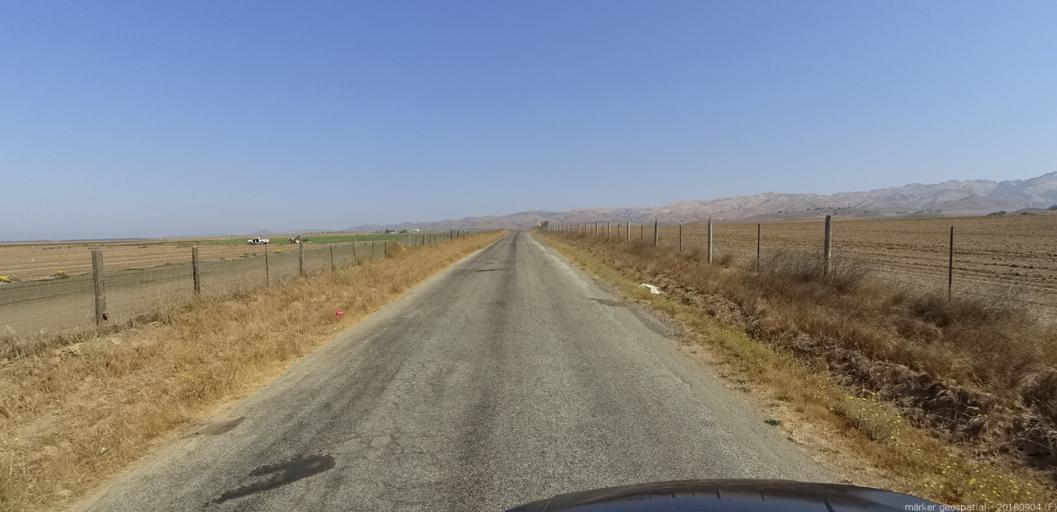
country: US
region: California
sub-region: Monterey County
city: Gonzales
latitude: 36.5010
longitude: -121.3648
